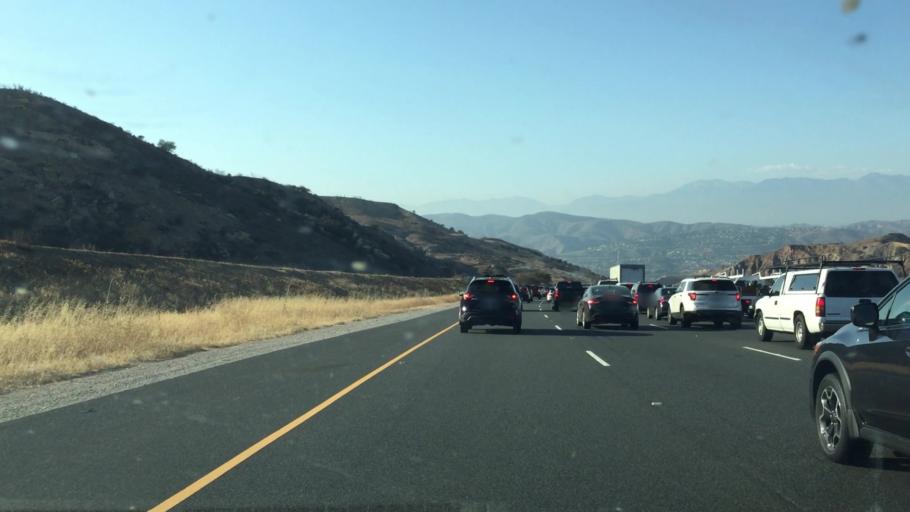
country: US
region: California
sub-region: Orange County
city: Villa Park
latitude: 33.8370
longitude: -117.7178
